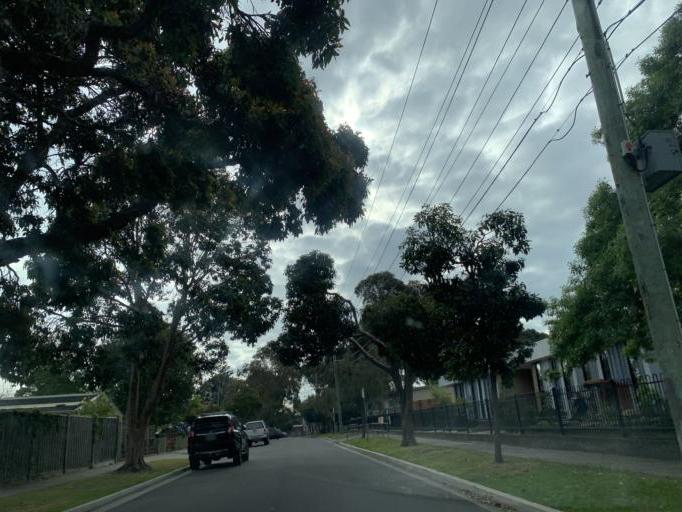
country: AU
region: Victoria
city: Beaumaris
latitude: -37.9859
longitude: 145.0377
